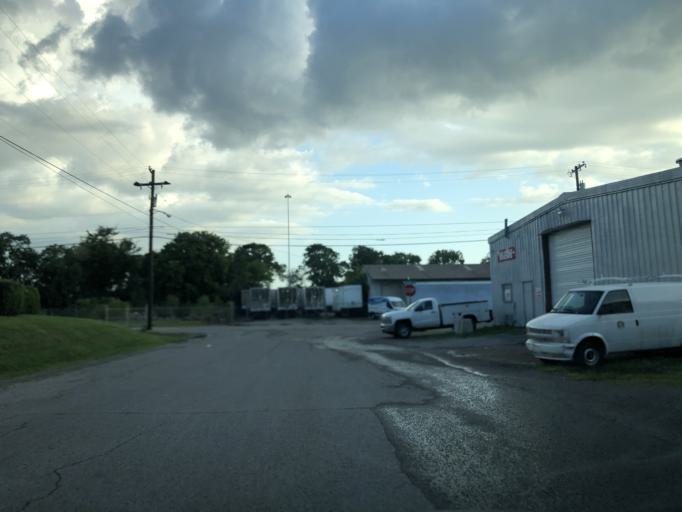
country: US
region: Tennessee
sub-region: Davidson County
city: Nashville
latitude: 36.1422
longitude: -86.7296
